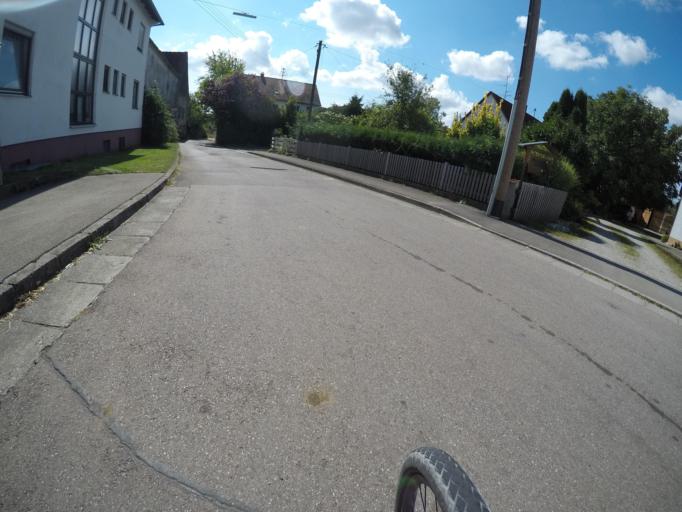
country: DE
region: Bavaria
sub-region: Swabia
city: Hochstadt an der Donau
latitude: 48.6187
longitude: 10.5359
